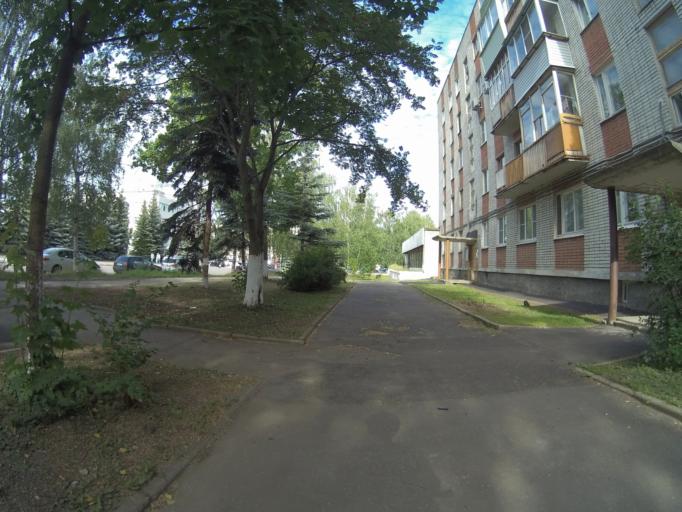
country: RU
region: Vladimir
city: Vladimir
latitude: 56.1505
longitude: 40.4320
